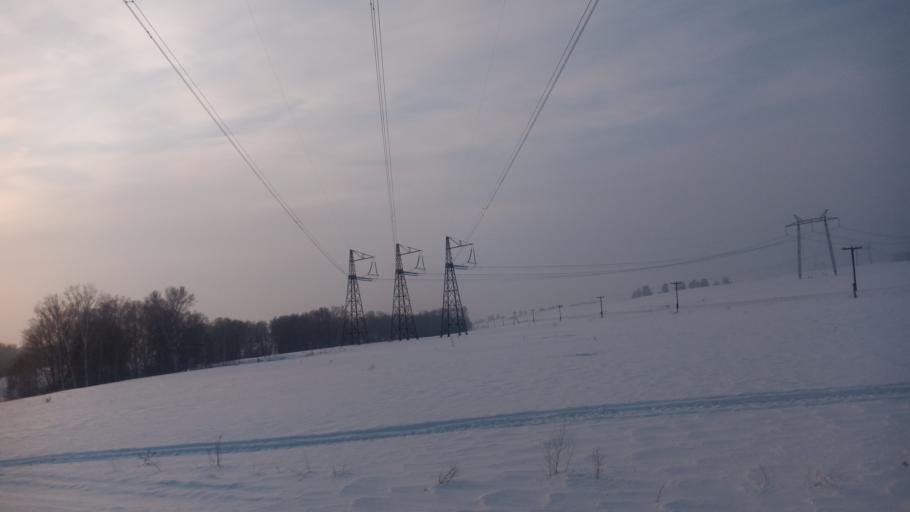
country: RU
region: Altai Krai
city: Nauchnyy Gorodok
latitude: 53.4055
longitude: 83.5143
